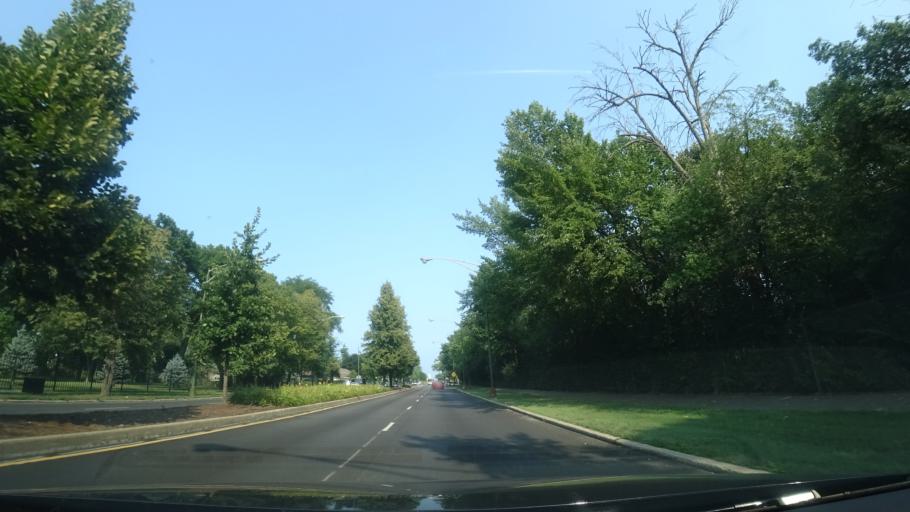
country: US
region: Illinois
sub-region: Cook County
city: Lincolnwood
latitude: 41.9901
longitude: -87.7232
